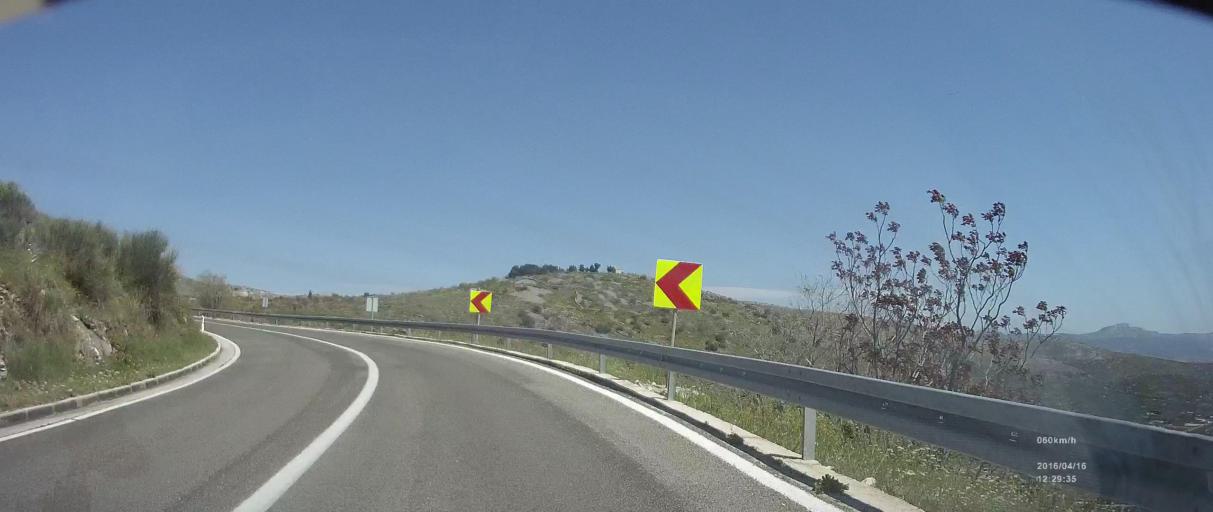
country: HR
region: Splitsko-Dalmatinska
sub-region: Grad Trogir
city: Trogir
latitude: 43.5250
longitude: 16.2198
